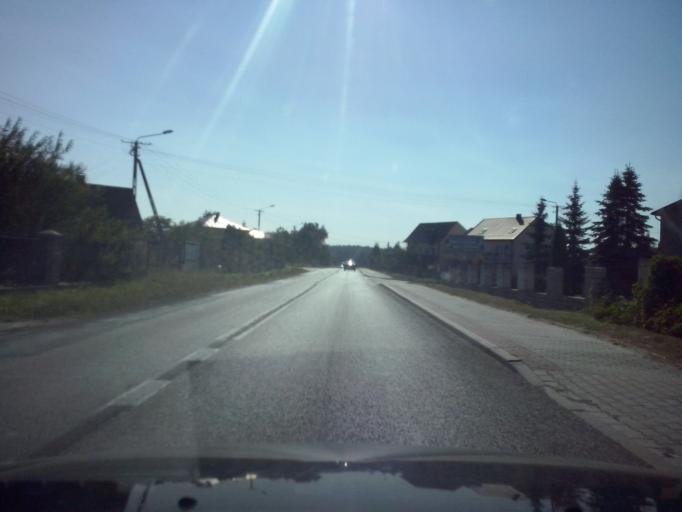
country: PL
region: Swietokrzyskie
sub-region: Powiat kielecki
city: Daleszyce
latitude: 50.8090
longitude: 20.7723
